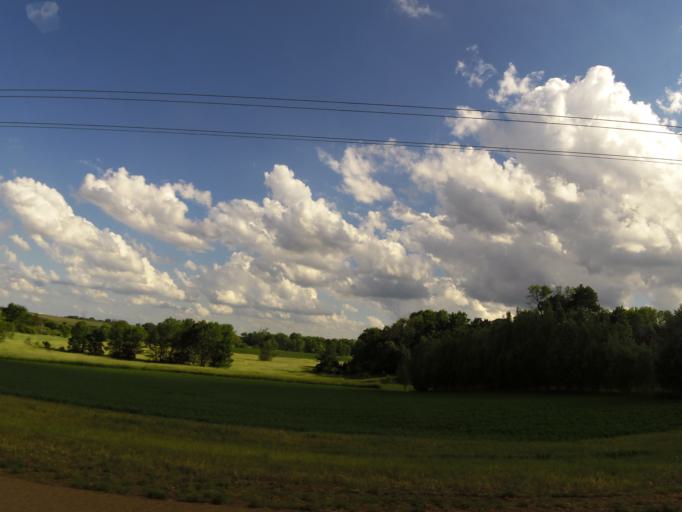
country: US
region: Minnesota
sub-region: Carver County
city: Victoria
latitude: 44.8192
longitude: -93.7012
